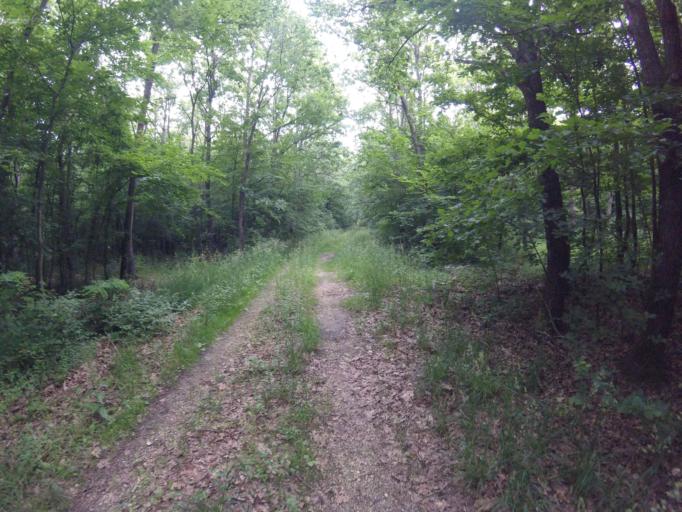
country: HU
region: Zala
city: Turje
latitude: 47.0417
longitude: 17.0241
